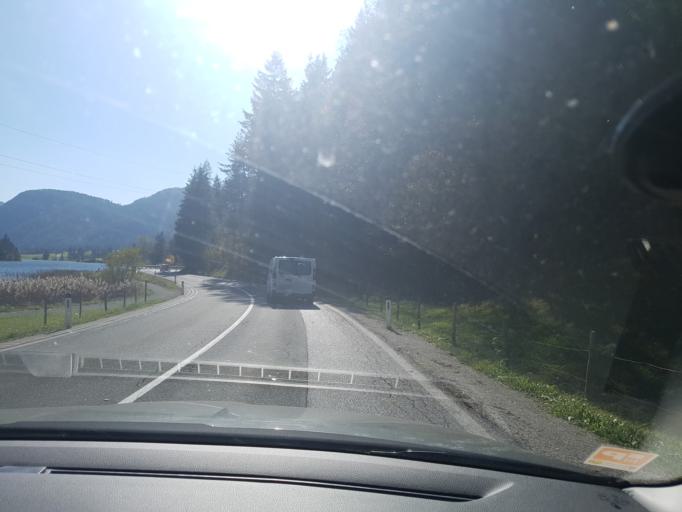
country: AT
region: Tyrol
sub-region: Politischer Bezirk Kitzbuhel
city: Waidring
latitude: 47.5466
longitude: 12.5682
